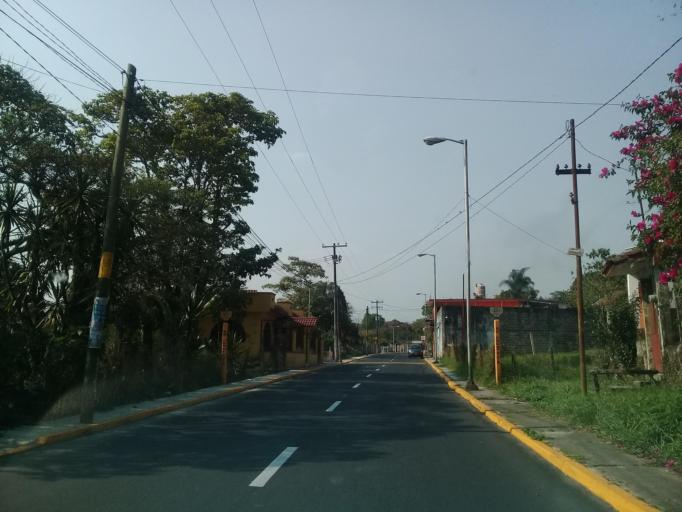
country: MX
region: Veracruz
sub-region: Ixtaczoquitlan
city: Campo Chico
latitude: 18.8475
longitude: -97.0366
